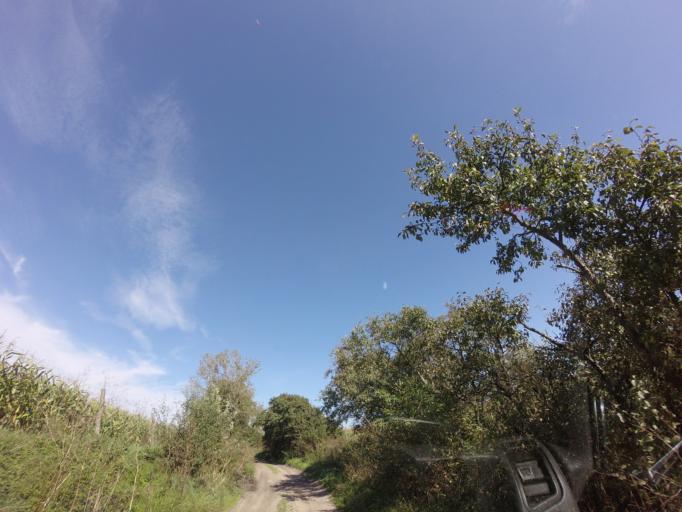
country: PL
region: West Pomeranian Voivodeship
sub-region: Powiat choszczenski
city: Recz
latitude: 53.2086
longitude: 15.4974
